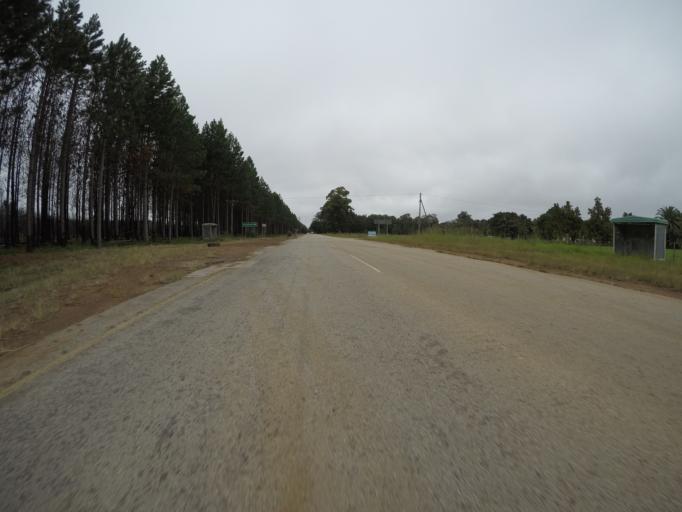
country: ZA
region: Eastern Cape
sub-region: Cacadu District Municipality
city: Kareedouw
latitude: -33.9907
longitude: 24.0846
